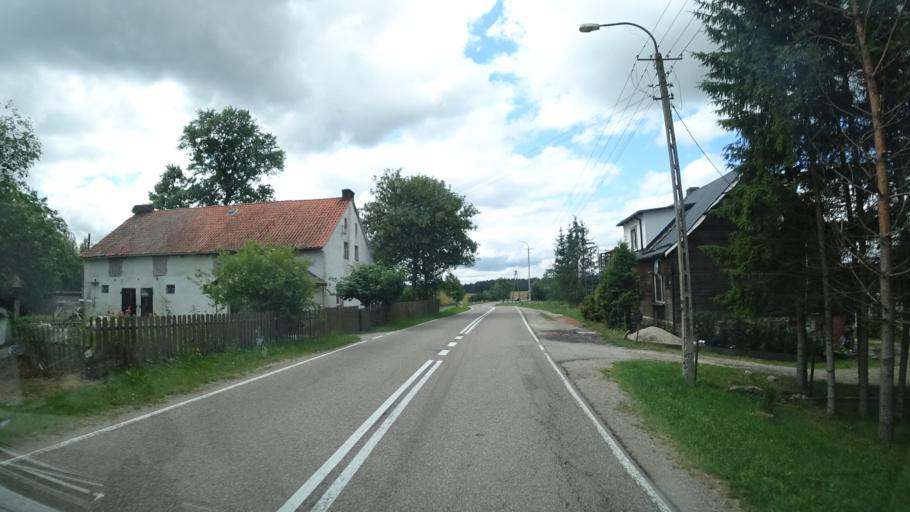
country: PL
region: Warmian-Masurian Voivodeship
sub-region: Powiat goldapski
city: Goldap
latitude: 54.2086
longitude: 22.1875
